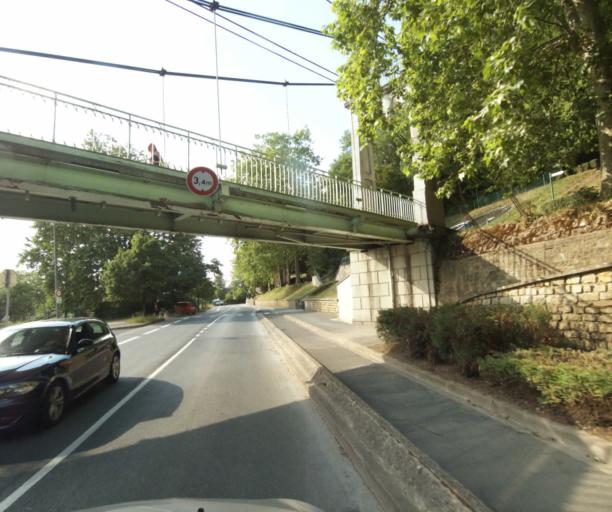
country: FR
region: Champagne-Ardenne
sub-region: Departement des Ardennes
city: Charleville-Mezieres
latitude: 49.7772
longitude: 4.7231
